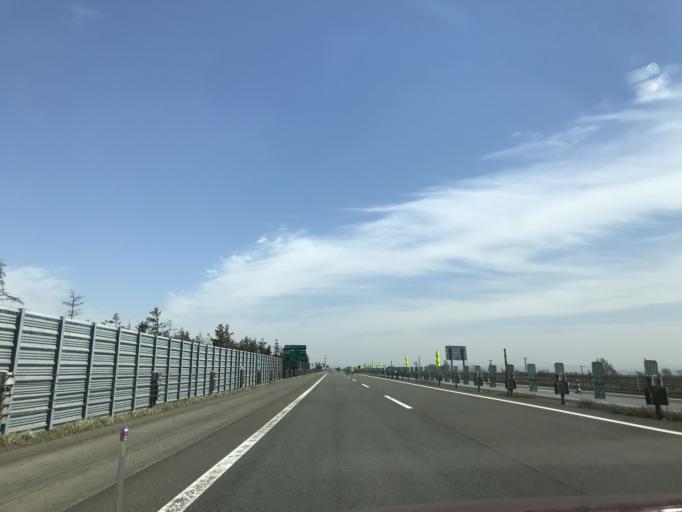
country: JP
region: Hokkaido
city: Ebetsu
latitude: 43.1109
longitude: 141.6112
